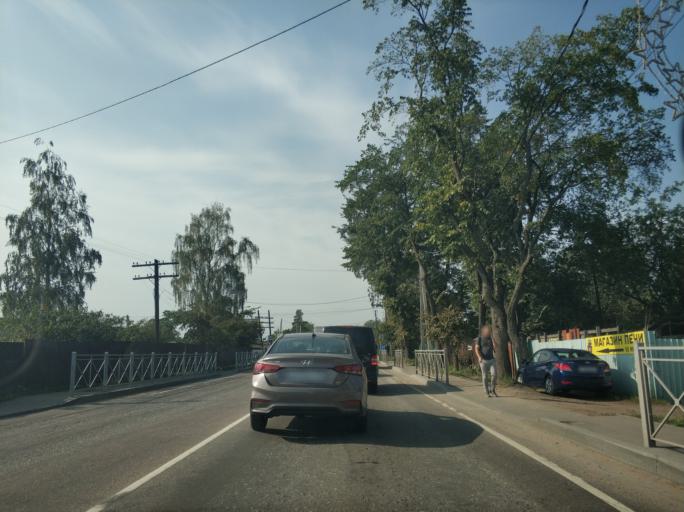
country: RU
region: Leningrad
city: Murino
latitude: 60.0462
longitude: 30.4527
